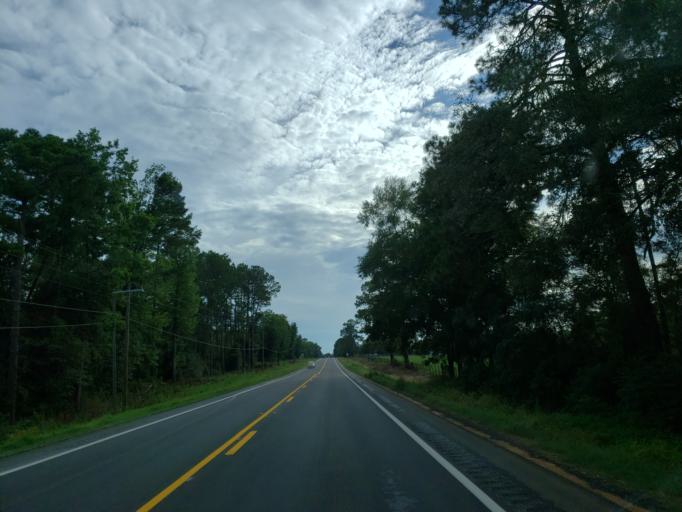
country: US
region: Georgia
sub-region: Irwin County
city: Ocilla
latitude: 31.5868
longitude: -83.2750
